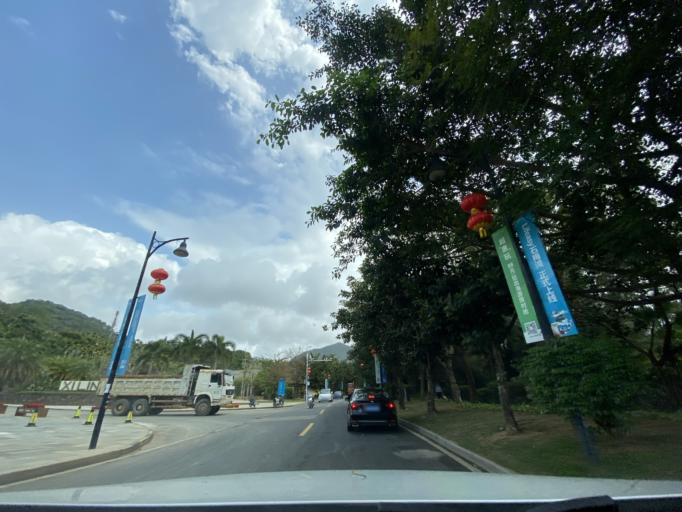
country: CN
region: Hainan
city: Liji
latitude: 18.6704
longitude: 110.2761
